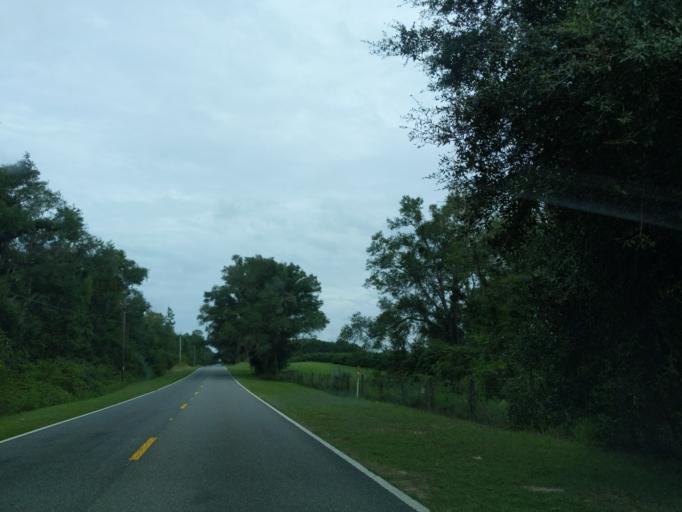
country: US
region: Florida
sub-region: Leon County
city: Woodville
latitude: 30.3726
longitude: -84.1995
